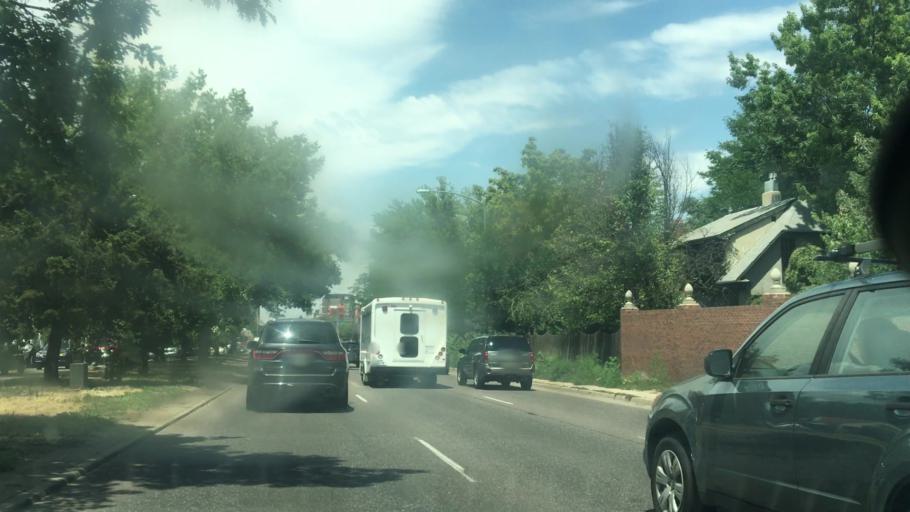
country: US
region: Colorado
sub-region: Arapahoe County
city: Glendale
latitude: 39.7260
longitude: -104.9407
